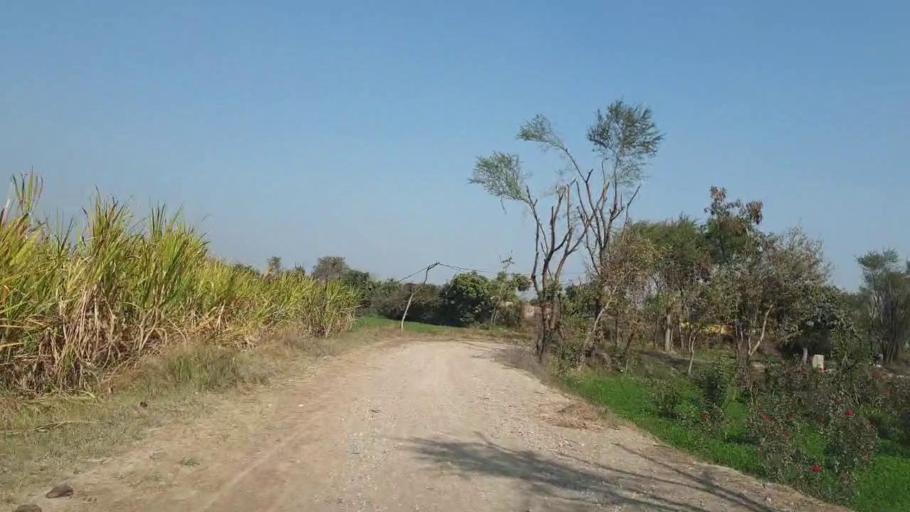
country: PK
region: Sindh
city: Matiari
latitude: 25.5058
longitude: 68.4491
